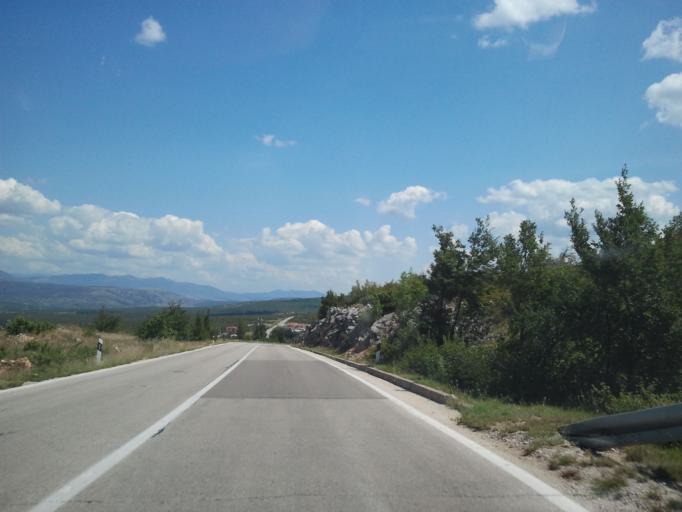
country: HR
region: Zadarska
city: Obrovac
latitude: 44.1958
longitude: 15.6702
